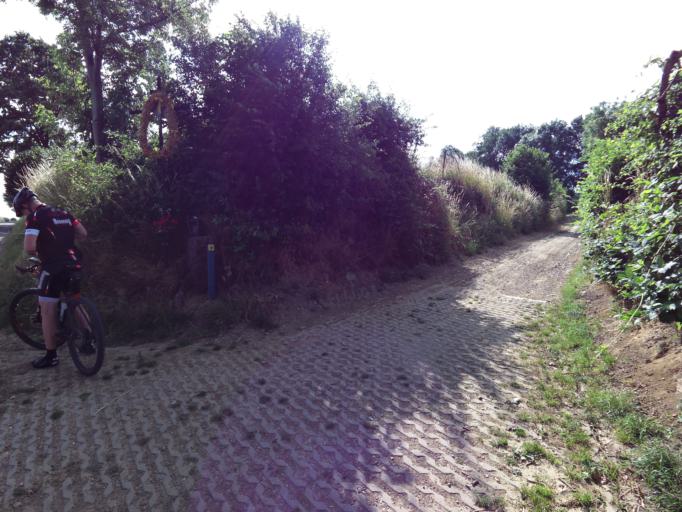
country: BE
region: Wallonia
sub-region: Province de Liege
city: Plombieres
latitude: 50.7848
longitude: 5.9328
